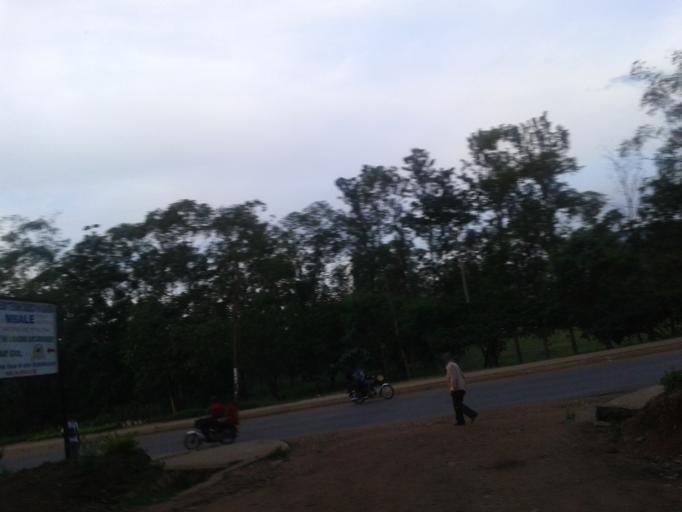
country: UG
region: Eastern Region
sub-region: Mbale District
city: Mbale
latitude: 1.0823
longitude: 34.1790
